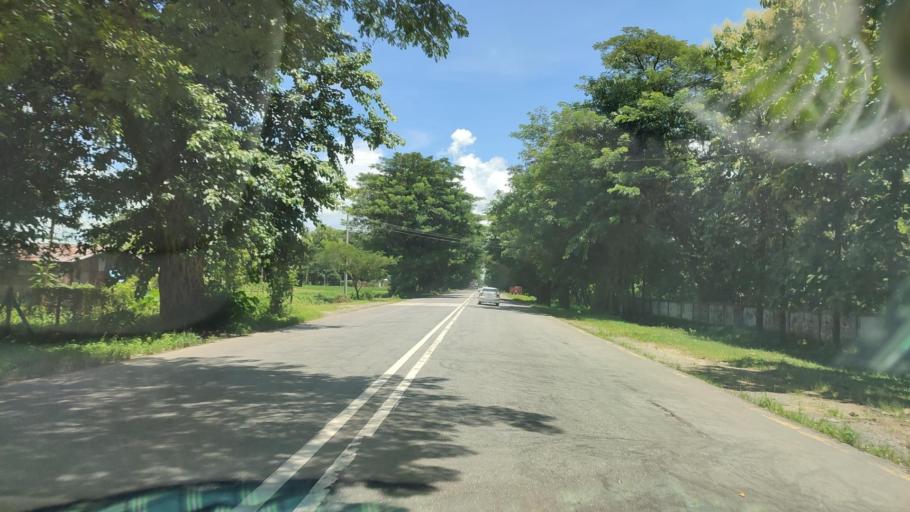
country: MM
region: Bago
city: Pyu
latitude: 18.2428
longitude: 96.5417
